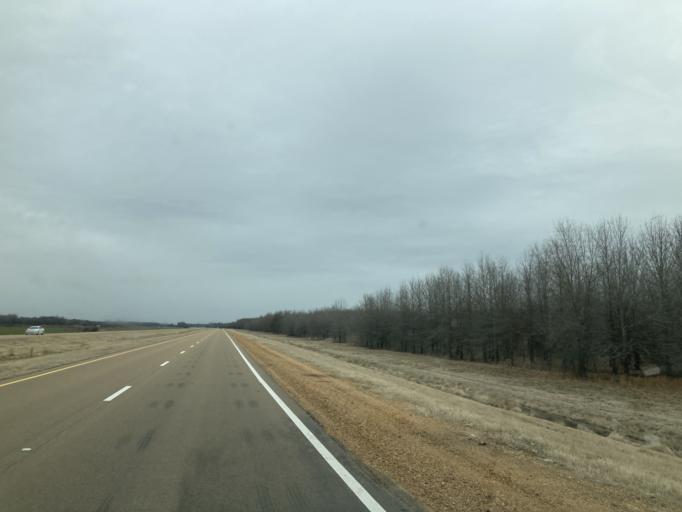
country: US
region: Mississippi
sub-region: Humphreys County
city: Belzoni
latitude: 33.0152
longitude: -90.4688
